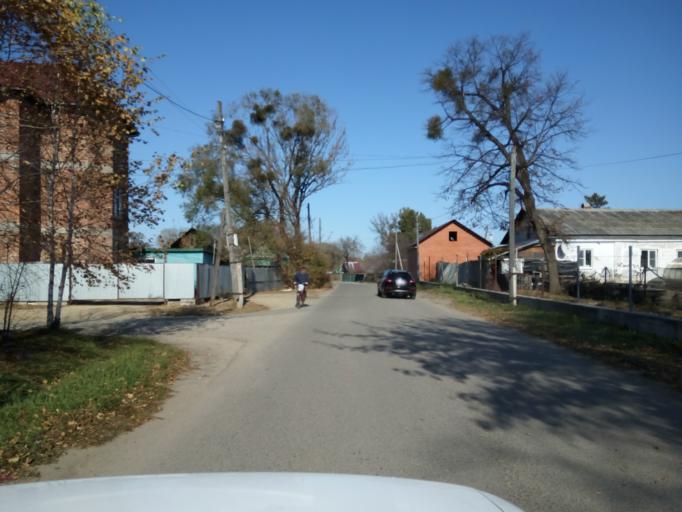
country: RU
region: Primorskiy
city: Dal'nerechensk
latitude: 45.9275
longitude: 133.7218
